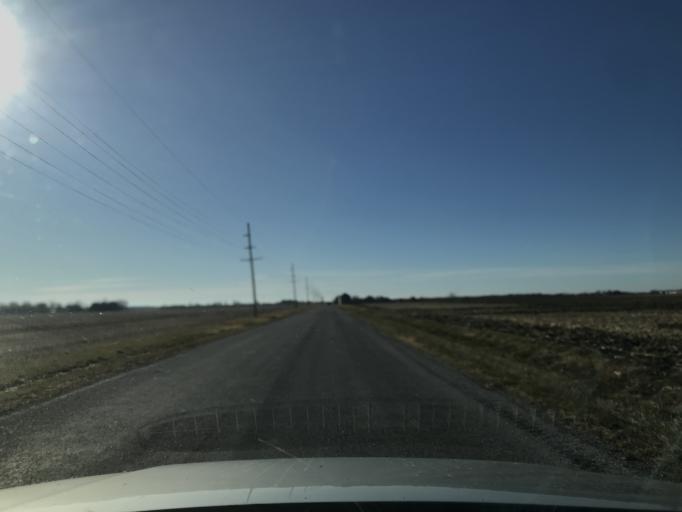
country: US
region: Illinois
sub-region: Hancock County
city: Carthage
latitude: 40.4761
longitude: -91.1782
